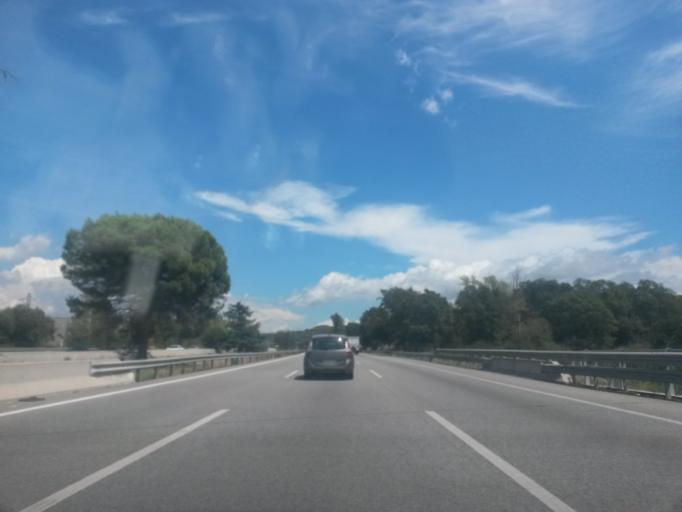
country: ES
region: Catalonia
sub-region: Provincia de Barcelona
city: Llinars del Valles
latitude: 41.6490
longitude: 2.4353
